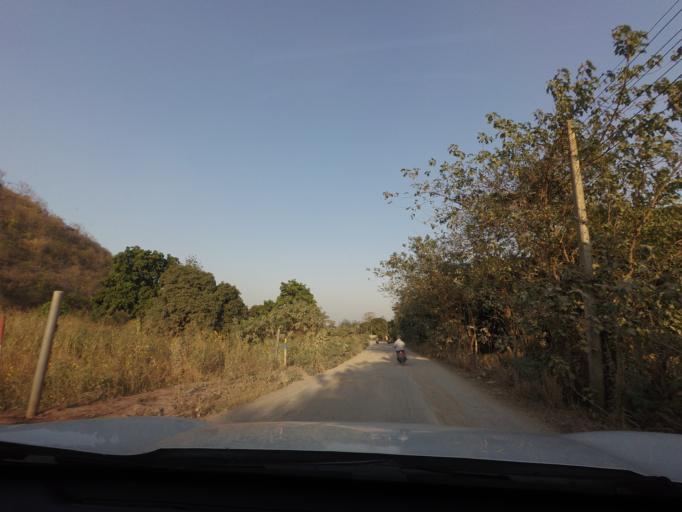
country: TH
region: Nakhon Ratchasima
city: Pak Chong
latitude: 14.6405
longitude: 101.3677
